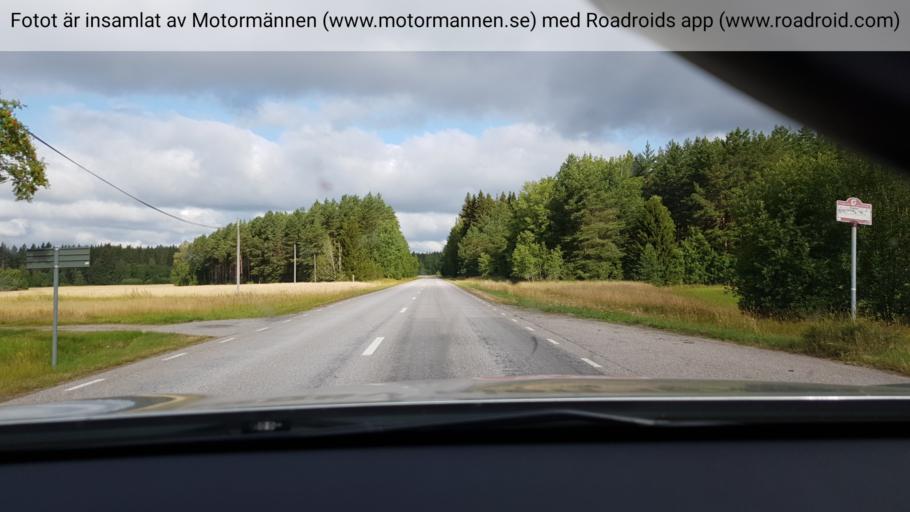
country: SE
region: Stockholm
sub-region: Norrtalje Kommun
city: Nykvarn
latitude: 59.9006
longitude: 18.3417
